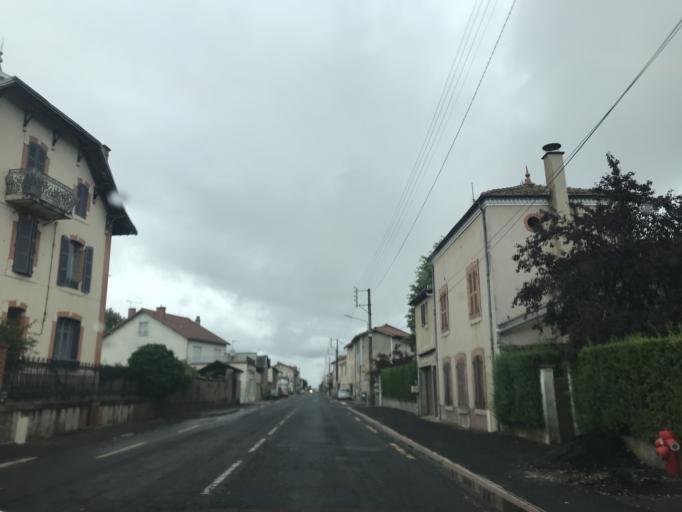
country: FR
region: Auvergne
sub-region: Departement du Puy-de-Dome
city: Marsac-en-Livradois
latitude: 45.4793
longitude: 3.7264
